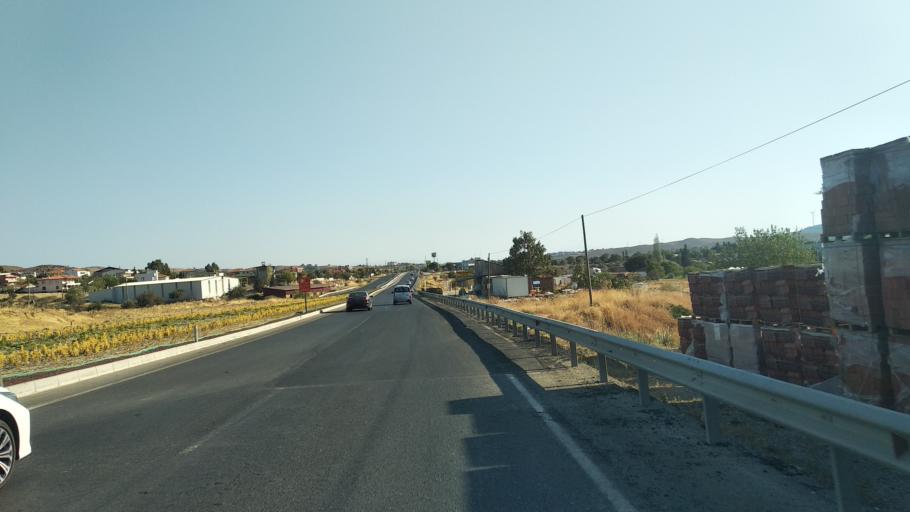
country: TR
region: Izmir
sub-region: Seferihisar
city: Seferhisar
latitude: 38.2540
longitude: 26.8320
